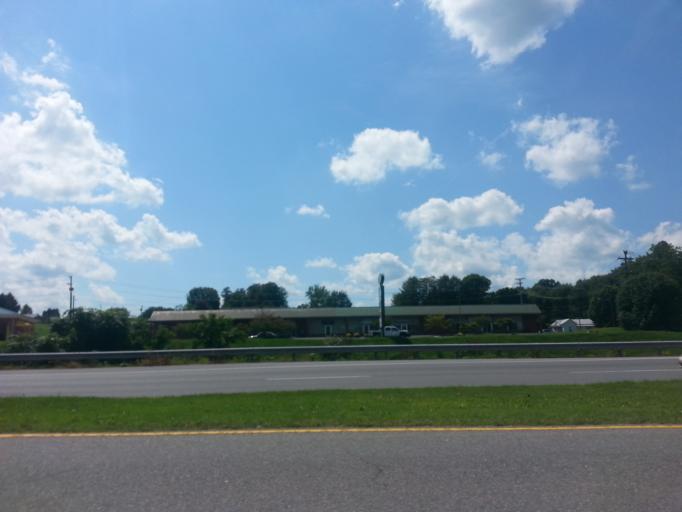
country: US
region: Virginia
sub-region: Washington County
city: Abingdon
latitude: 36.7101
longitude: -81.9972
